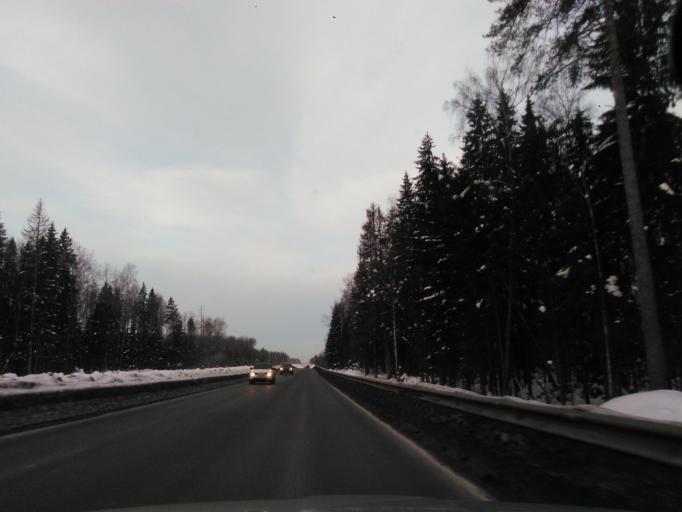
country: RU
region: Moskovskaya
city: Povarovo
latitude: 56.0383
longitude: 37.0865
